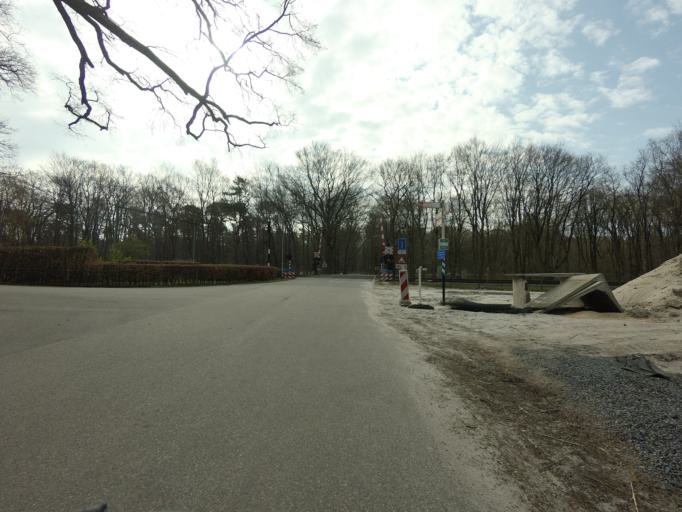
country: NL
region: Gelderland
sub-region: Gemeente Harderwijk
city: Harderwijk
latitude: 52.3449
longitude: 5.7057
